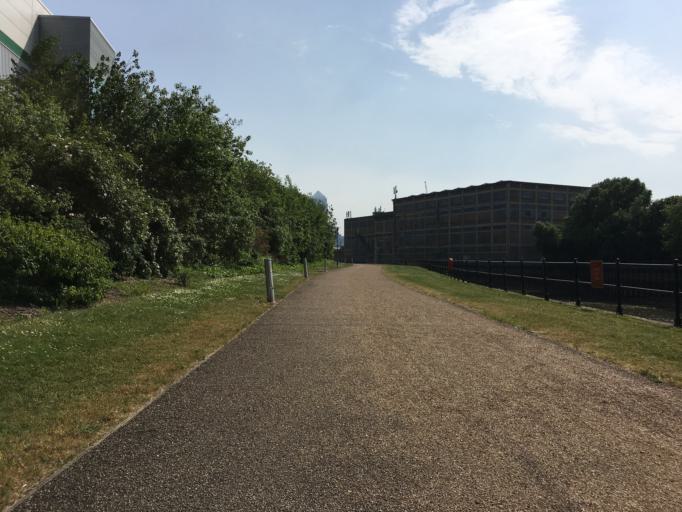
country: GB
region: England
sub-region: Greater London
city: Poplar
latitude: 51.5217
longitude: -0.0077
